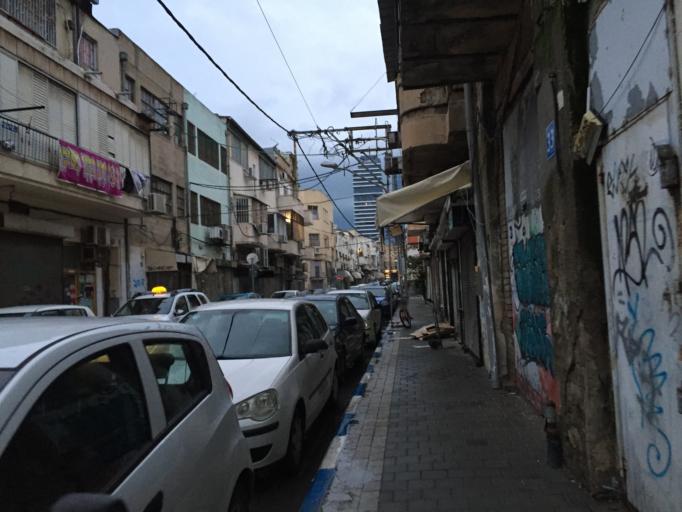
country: IL
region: Tel Aviv
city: Yafo
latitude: 32.0581
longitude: 34.7699
